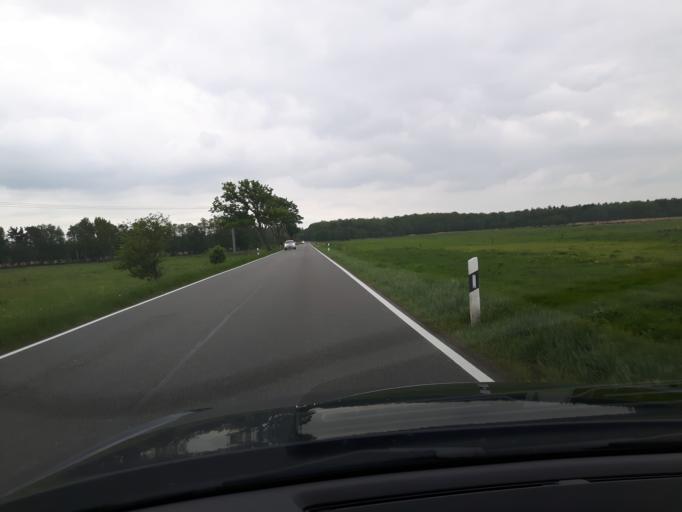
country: DE
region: Mecklenburg-Vorpommern
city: Ostseebad Prerow
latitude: 54.4050
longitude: 12.5697
